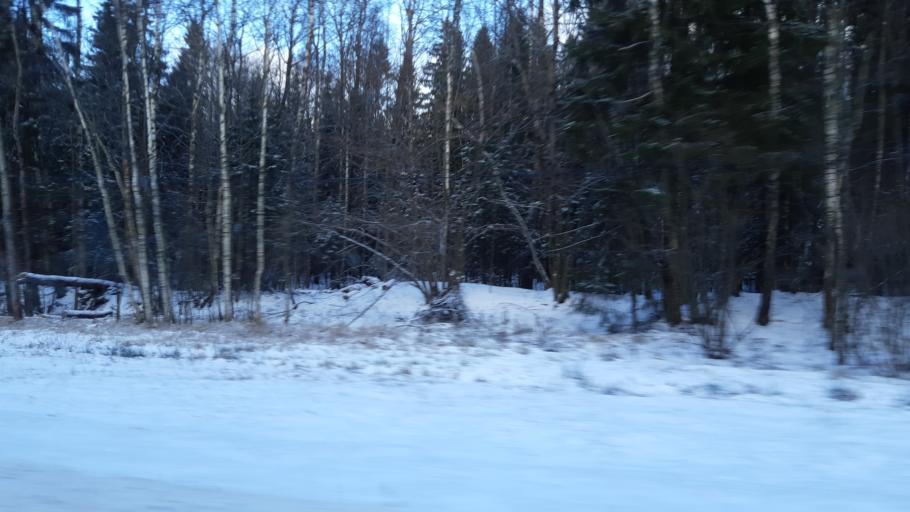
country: RU
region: Moskovskaya
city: Svatkovo
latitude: 56.3205
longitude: 38.2964
